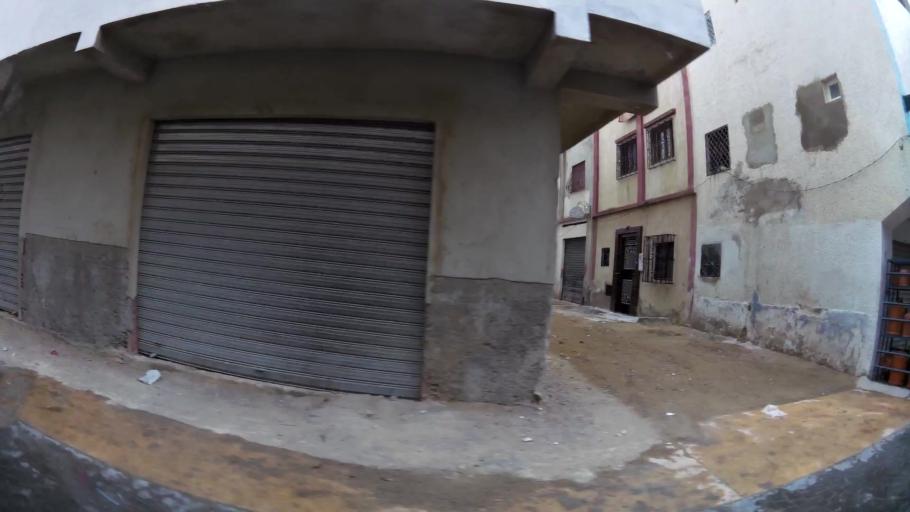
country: MA
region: Tanger-Tetouan
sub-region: Tetouan
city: Martil
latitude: 35.6267
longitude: -5.2841
